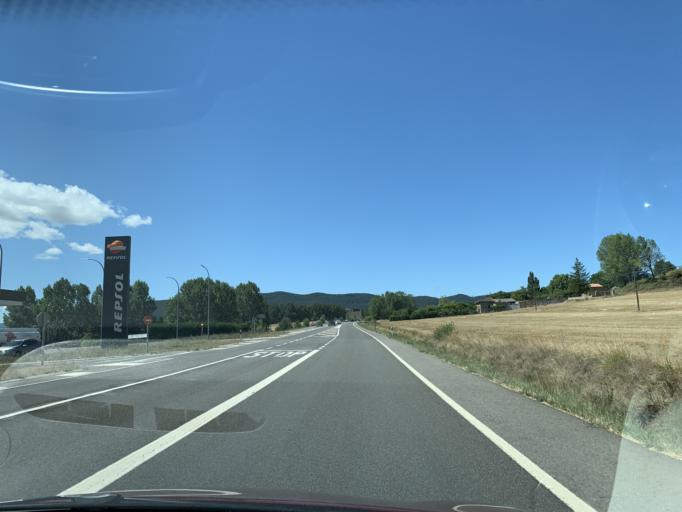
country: ES
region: Aragon
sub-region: Provincia de Huesca
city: Sabinanigo
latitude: 42.5403
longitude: -0.3554
